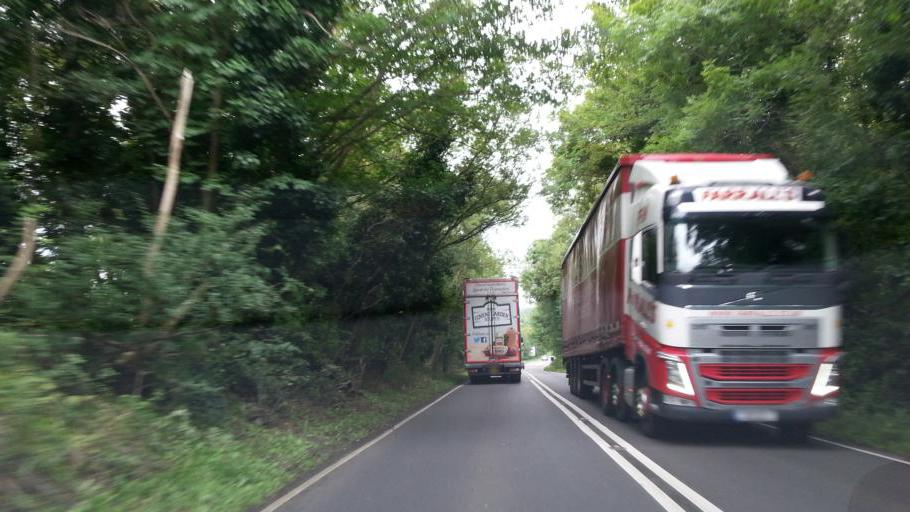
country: GB
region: England
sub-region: Cambridgeshire
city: Papworth Everard
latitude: 52.2797
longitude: -0.1400
